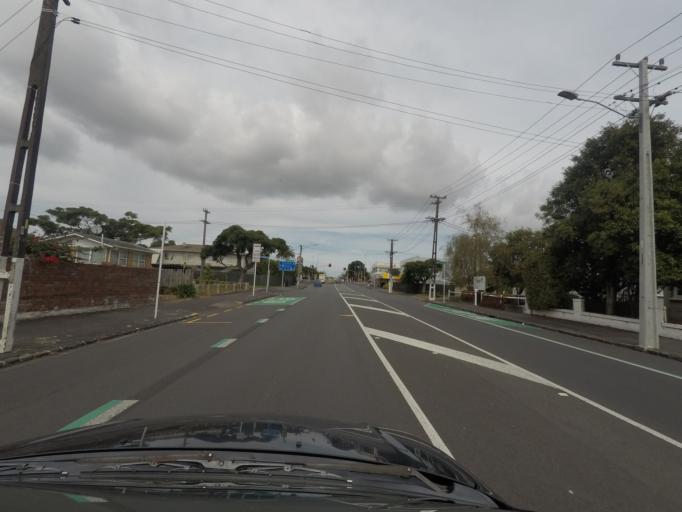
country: NZ
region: Auckland
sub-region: Auckland
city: Auckland
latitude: -36.8838
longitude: 174.7389
